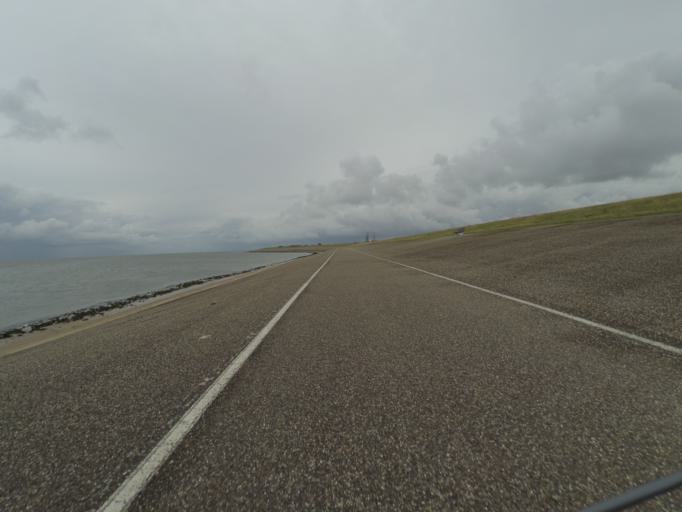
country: NL
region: North Holland
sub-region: Gemeente Den Helder
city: Den Helder
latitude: 52.9641
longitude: 4.7499
